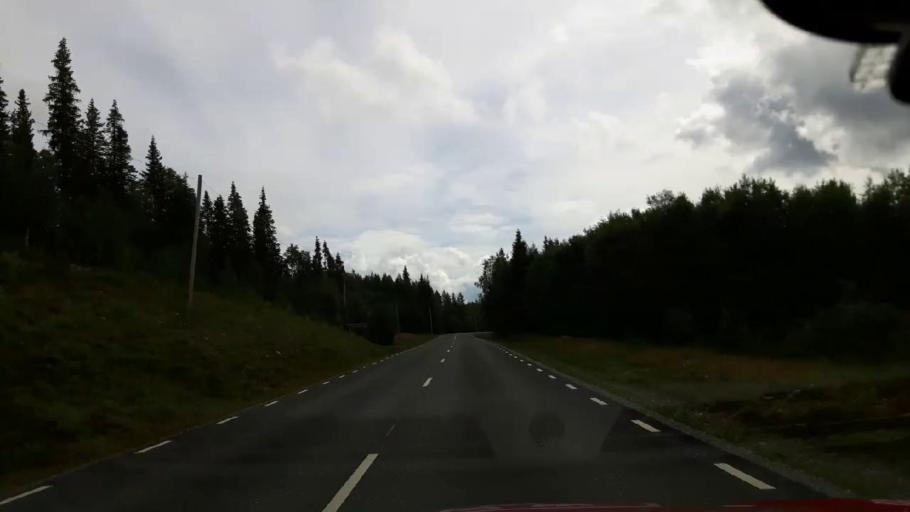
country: NO
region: Nord-Trondelag
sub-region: Lierne
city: Sandvika
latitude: 64.5887
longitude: 14.1203
